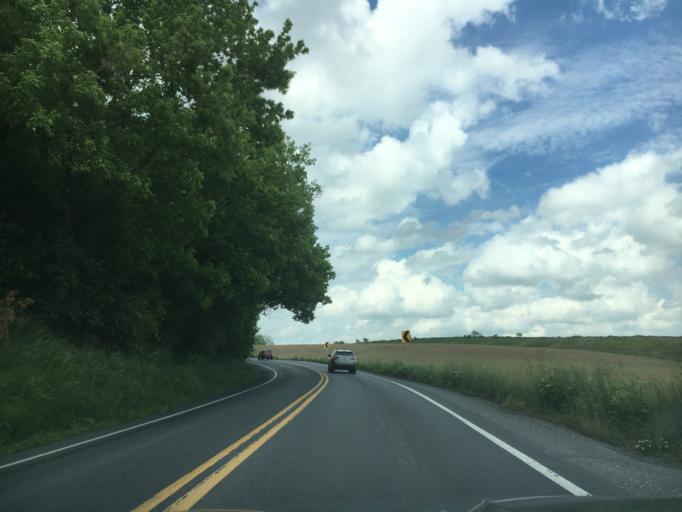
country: US
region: Pennsylvania
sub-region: Lehigh County
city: Egypt
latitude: 40.6644
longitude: -75.5394
